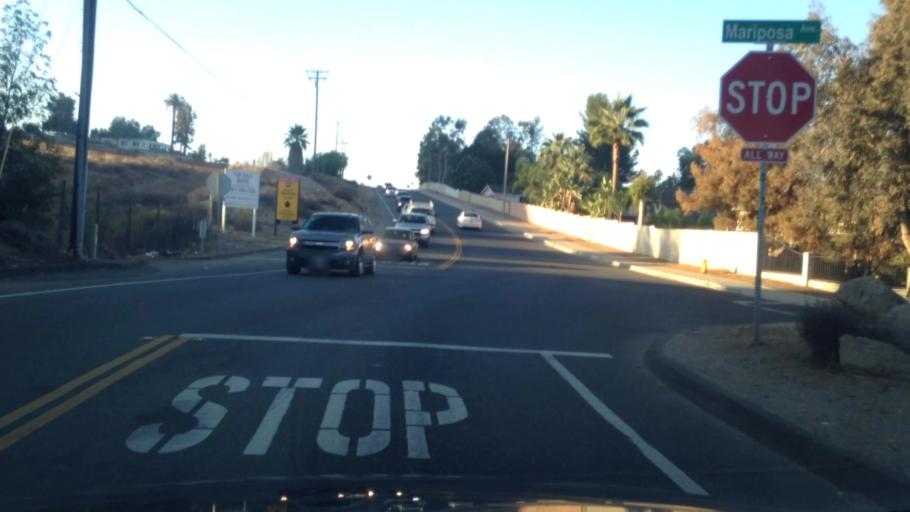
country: US
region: California
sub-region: Riverside County
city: Woodcrest
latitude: 33.8728
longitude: -117.3661
